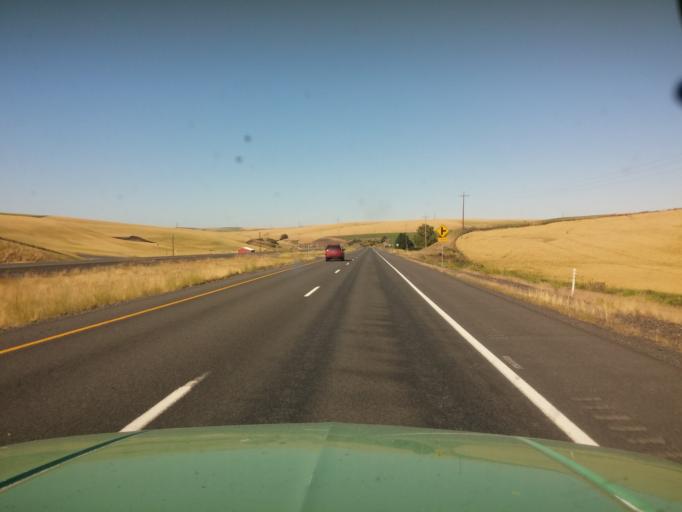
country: US
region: Idaho
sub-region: Nez Perce County
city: Lewiston
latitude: 46.4910
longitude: -117.0205
